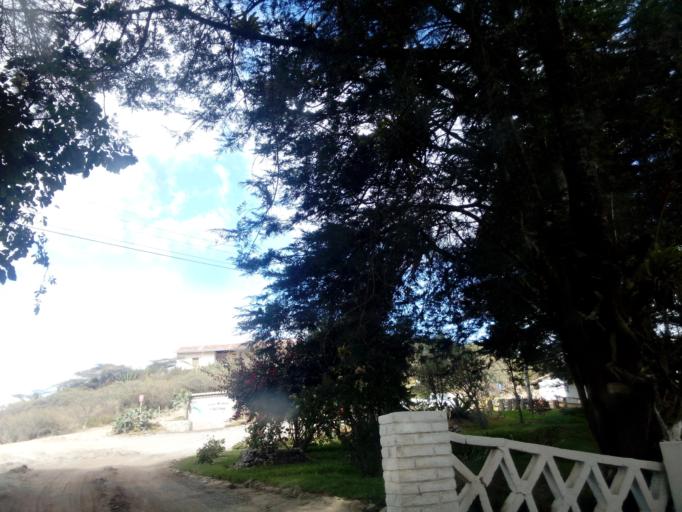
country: EC
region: Imbabura
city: Atuntaqui
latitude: 0.4182
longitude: -78.1890
